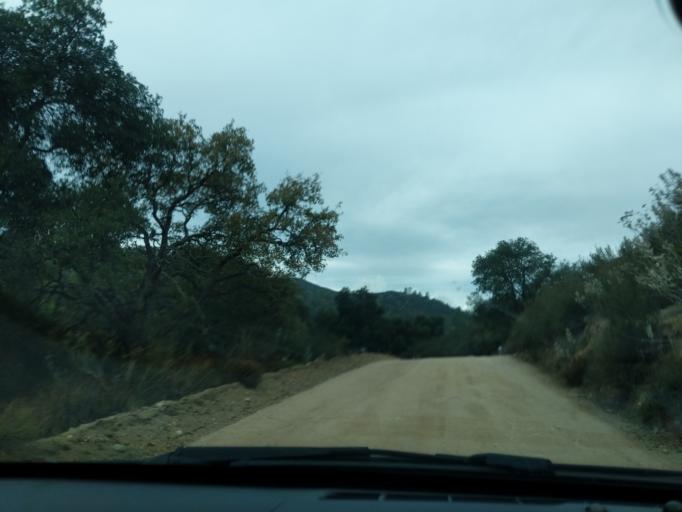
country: US
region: California
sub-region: Monterey County
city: Soledad
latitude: 36.5659
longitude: -121.2081
